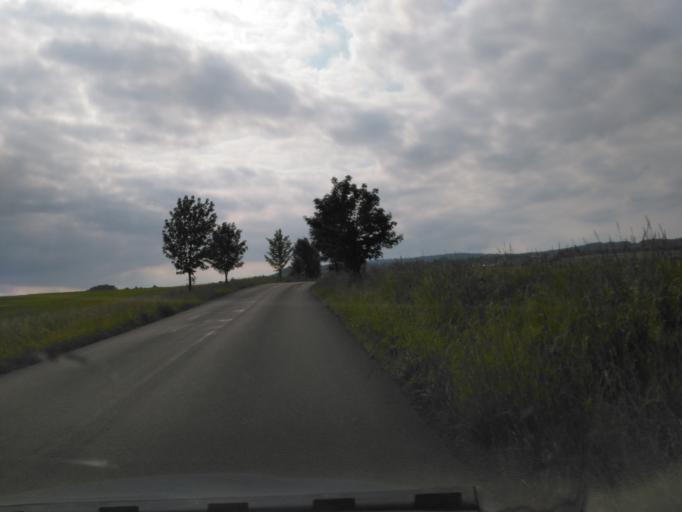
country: CZ
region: Central Bohemia
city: Hudlice
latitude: 49.9579
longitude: 13.9929
